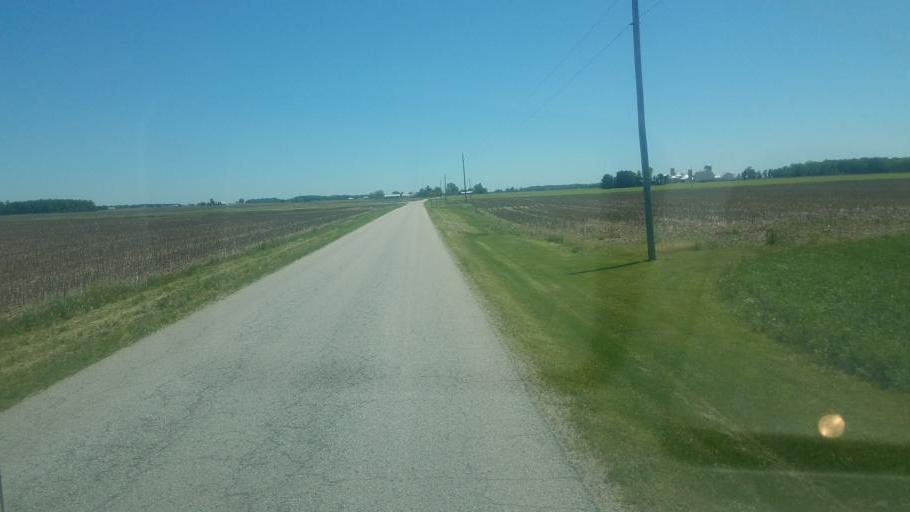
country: US
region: Ohio
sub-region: Shelby County
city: Sidney
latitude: 40.2035
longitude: -84.0777
